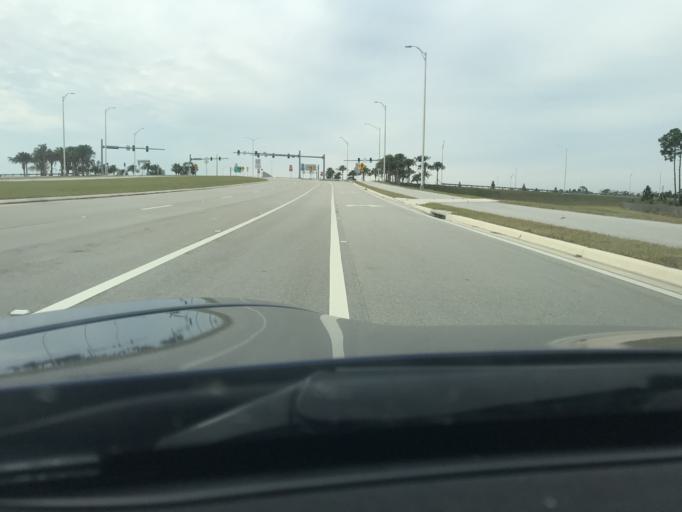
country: US
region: Florida
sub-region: Brevard County
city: Grant-Valkaria
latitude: 27.8962
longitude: -80.5922
